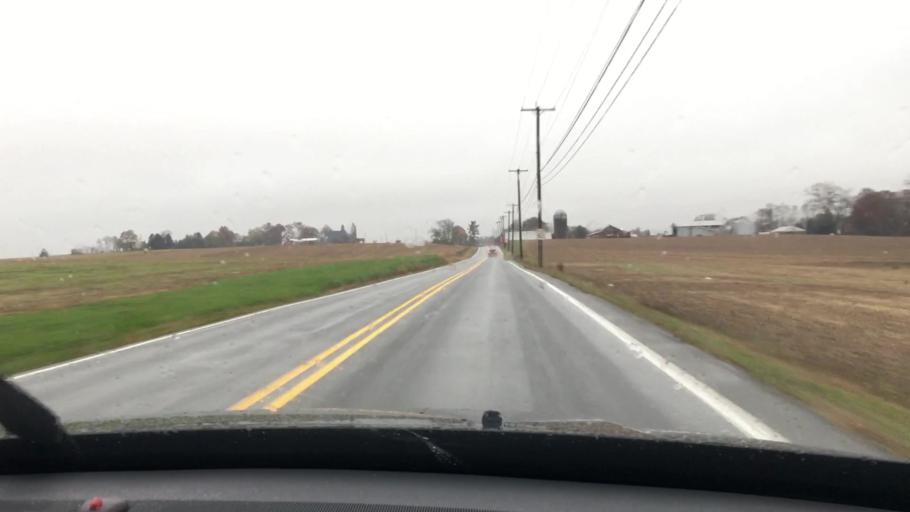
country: US
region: Pennsylvania
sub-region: York County
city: Stewartstown
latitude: 39.7287
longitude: -76.5166
